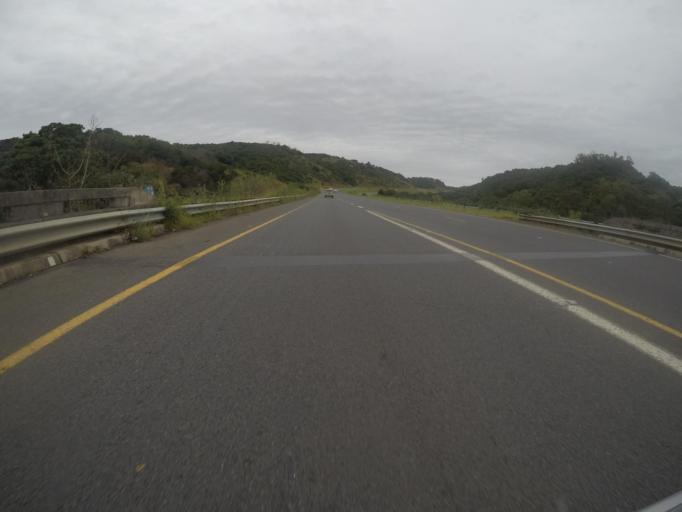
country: ZA
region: Eastern Cape
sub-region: Buffalo City Metropolitan Municipality
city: East London
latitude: -32.9663
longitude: 27.9176
